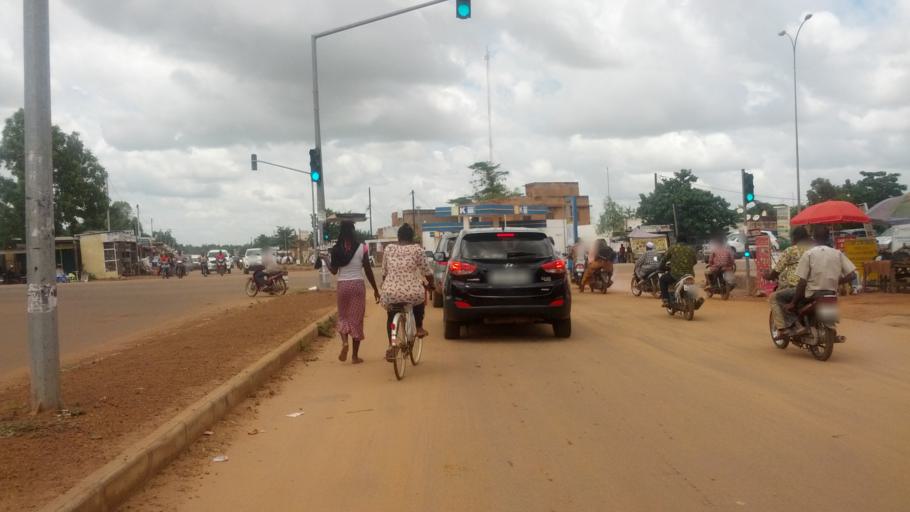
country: BF
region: Centre
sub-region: Kadiogo Province
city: Ouagadougou
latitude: 12.3757
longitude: -1.4967
